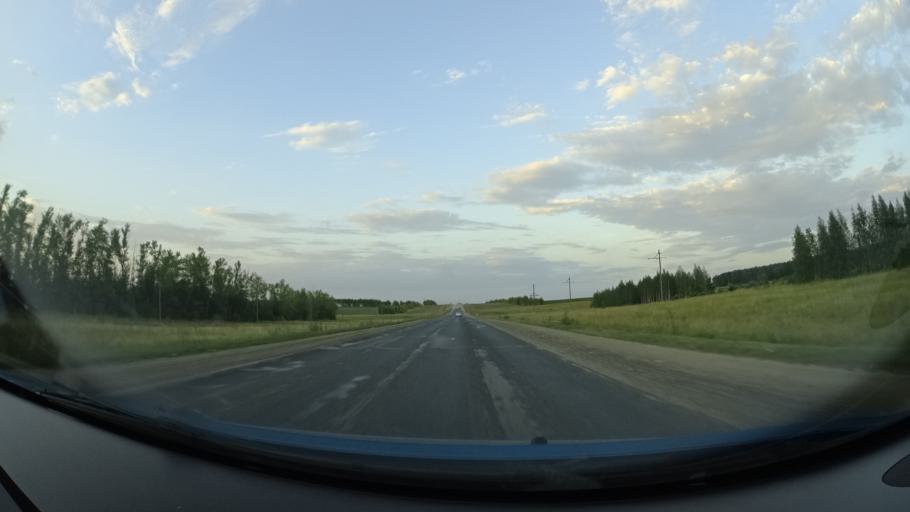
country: RU
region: Orenburg
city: Severnoye
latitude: 54.2218
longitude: 52.7387
